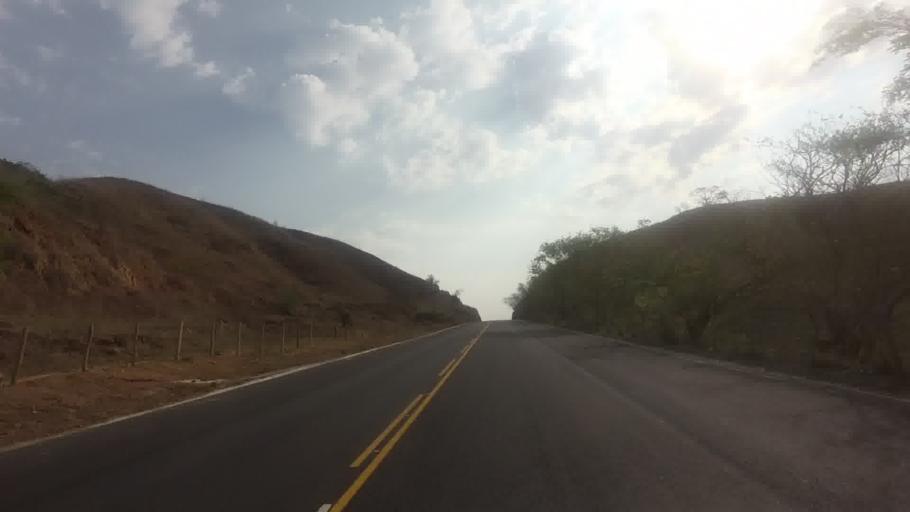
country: BR
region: Rio de Janeiro
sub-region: Itaperuna
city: Itaperuna
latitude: -21.2948
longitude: -41.8295
